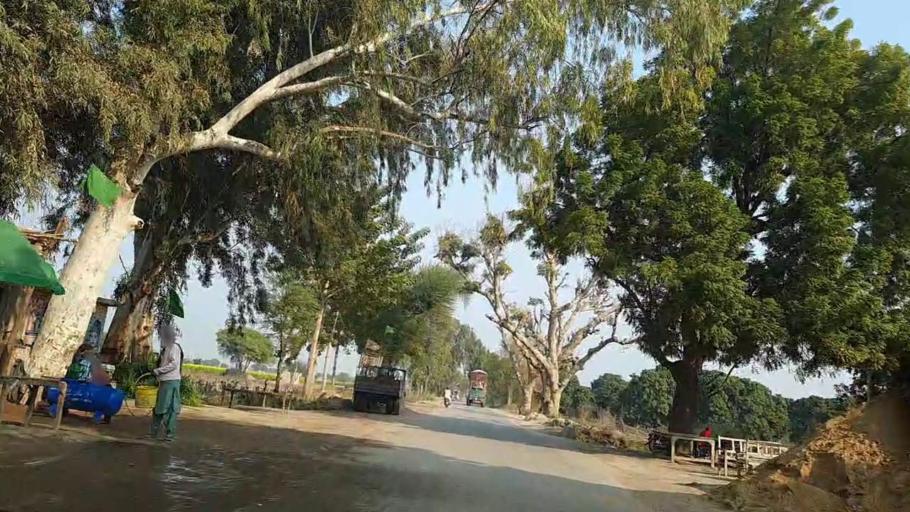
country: PK
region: Sindh
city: Sakrand
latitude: 26.1321
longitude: 68.2196
